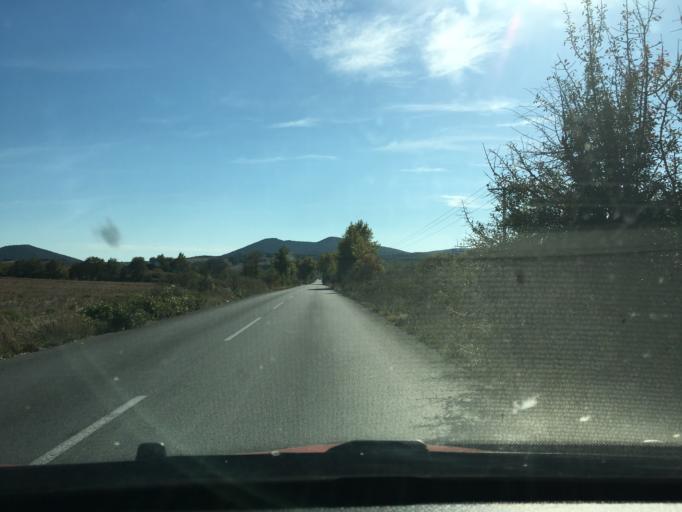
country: GR
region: Central Macedonia
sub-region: Nomos Chalkidikis
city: Megali Panagia
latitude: 40.3750
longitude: 23.6953
